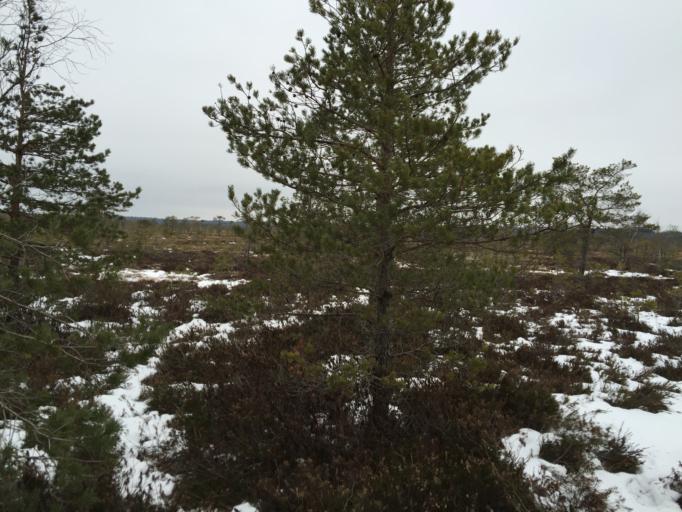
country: LV
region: Saulkrastu
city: Saulkrasti
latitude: 57.2297
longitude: 24.5036
